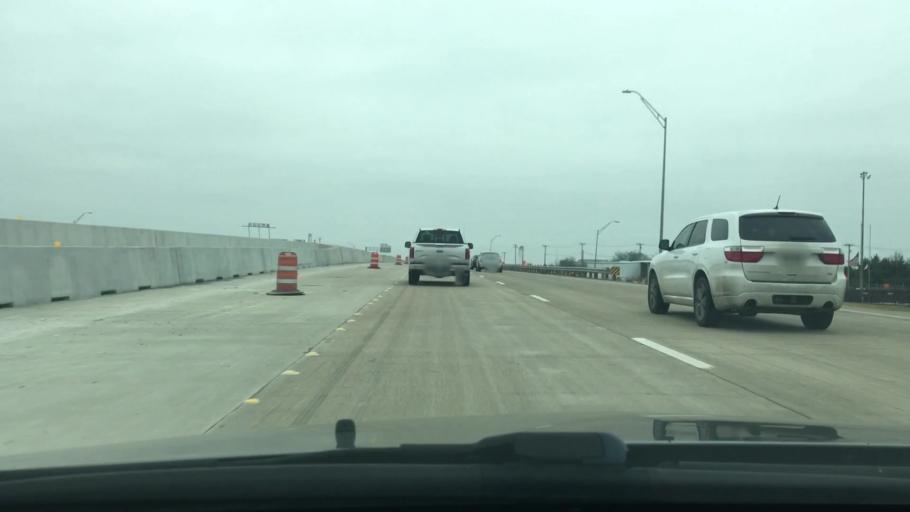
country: US
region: Texas
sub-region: Navarro County
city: Corsicana
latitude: 32.0612
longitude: -96.4524
